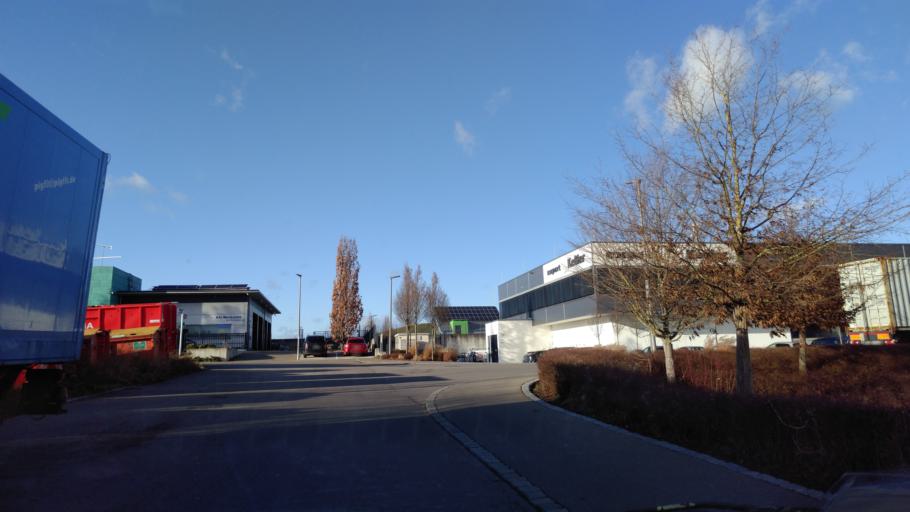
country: DE
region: Baden-Wuerttemberg
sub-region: Tuebingen Region
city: Bad Waldsee
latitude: 47.9133
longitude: 9.7420
